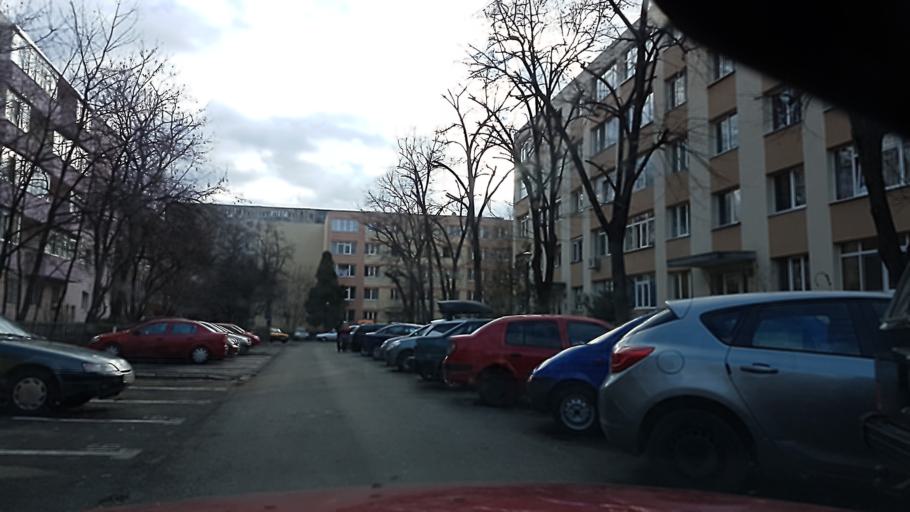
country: RO
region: Ilfov
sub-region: Comuna Popesti-Leordeni
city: Popesti-Leordeni
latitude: 44.4124
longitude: 26.1772
